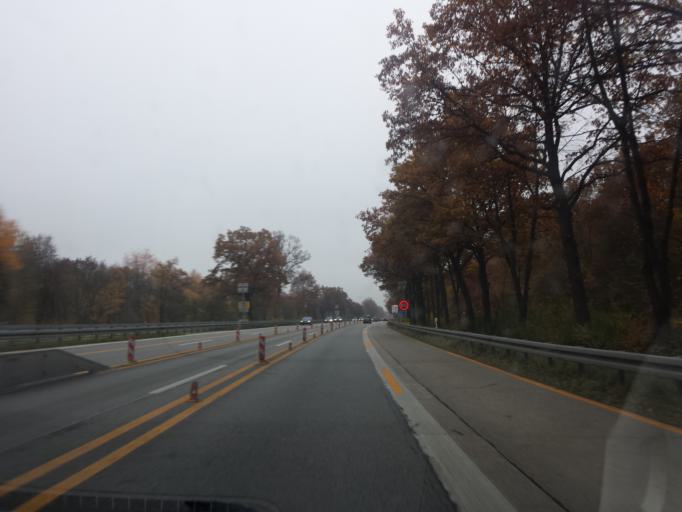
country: DE
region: Bavaria
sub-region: Upper Bavaria
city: Neuried
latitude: 48.0758
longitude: 11.4860
